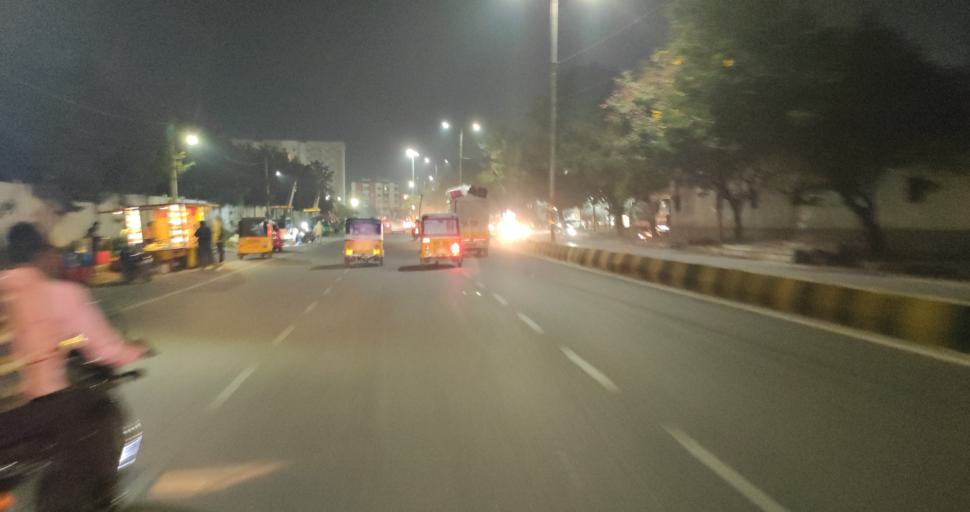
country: IN
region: Telangana
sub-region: Rangareddi
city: Gaddi Annaram
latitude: 17.3666
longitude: 78.5017
